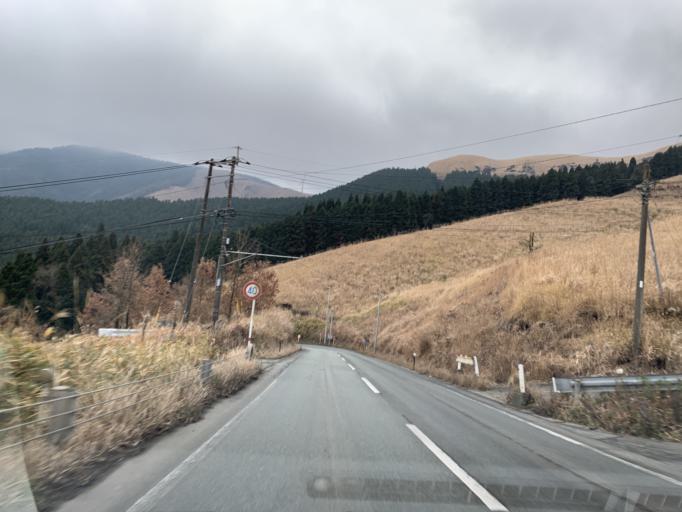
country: JP
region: Kumamoto
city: Aso
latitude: 32.9161
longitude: 130.9720
